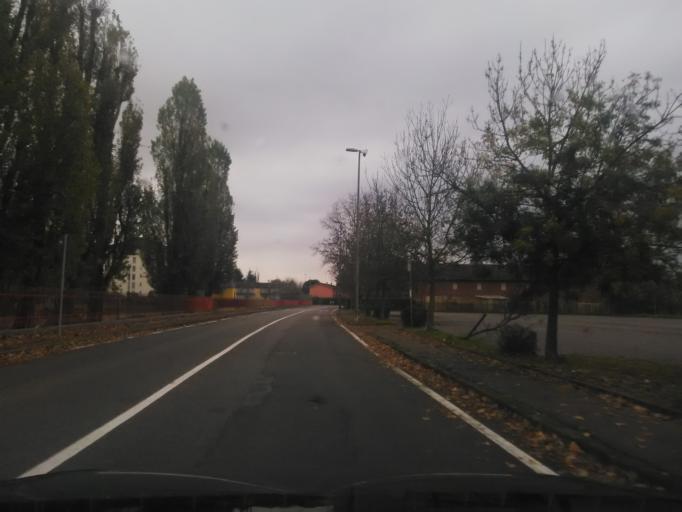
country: IT
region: Piedmont
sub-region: Provincia di Vercelli
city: Vercelli
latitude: 45.3179
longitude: 8.4009
